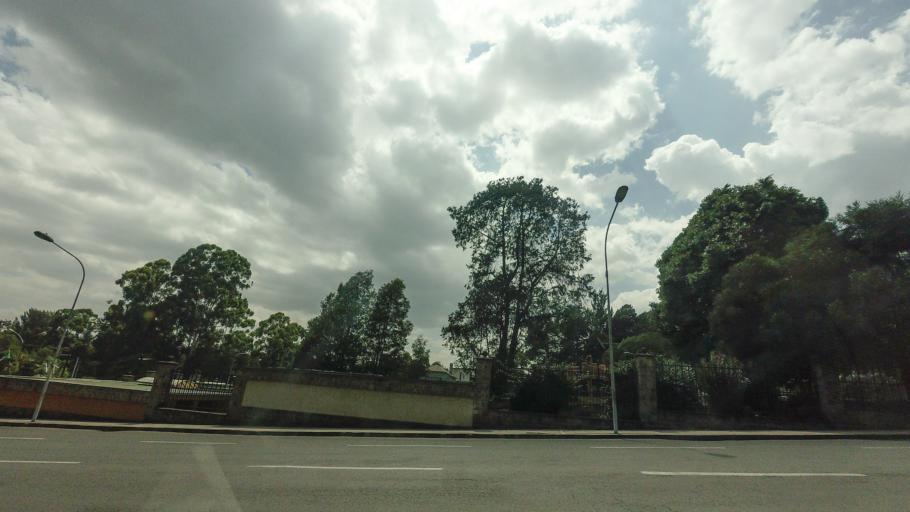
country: ET
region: Adis Abeba
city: Addis Ababa
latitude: 9.0182
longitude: 38.7637
